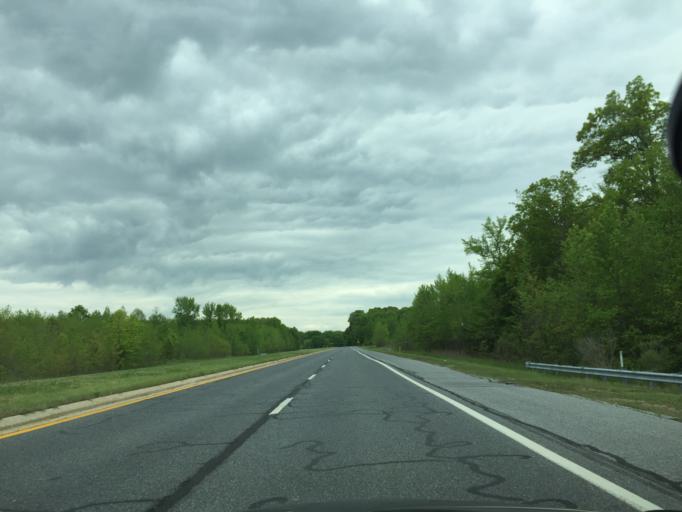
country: US
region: Maryland
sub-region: Baltimore County
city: Middle River
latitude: 39.2966
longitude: -76.4372
